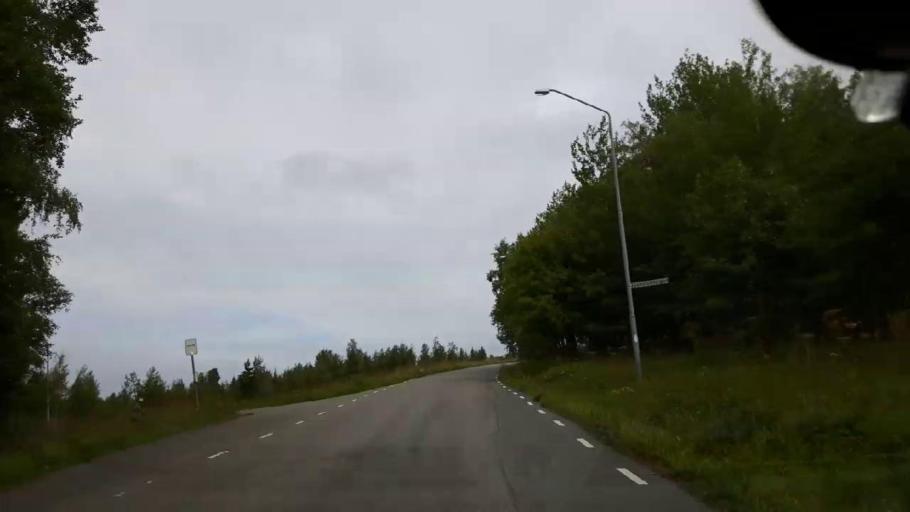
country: SE
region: Jaemtland
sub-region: OEstersunds Kommun
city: Ostersund
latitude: 63.1763
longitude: 14.5166
